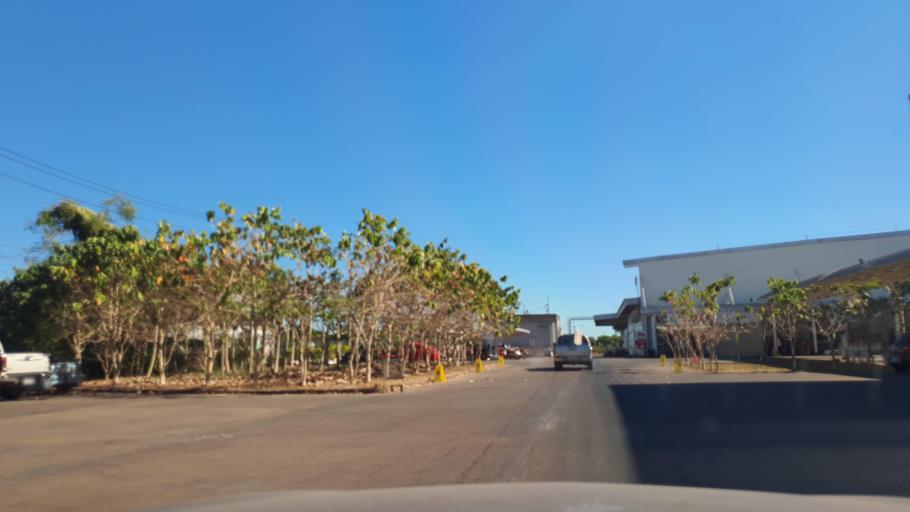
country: TH
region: Nakhon Phanom
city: Nakhon Phanom
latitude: 17.3890
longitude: 104.7671
